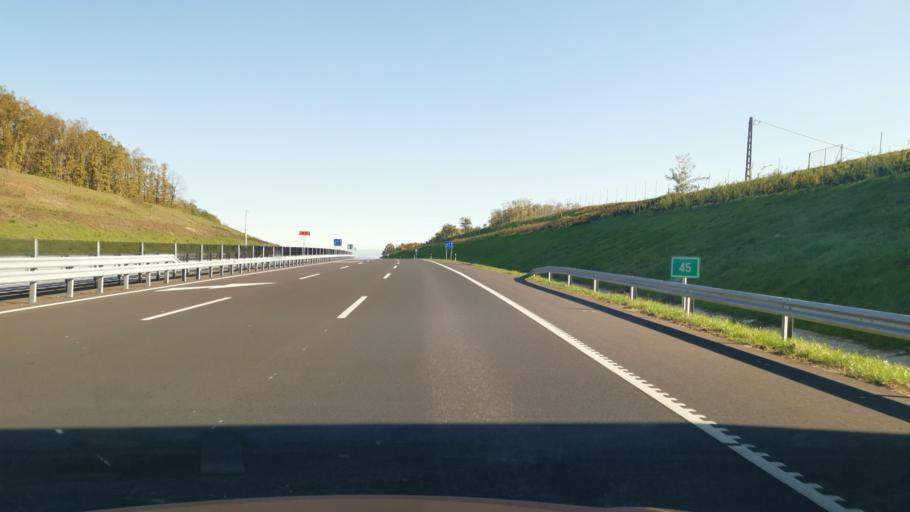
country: HU
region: Borsod-Abauj-Zemplen
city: Szikszo
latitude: 48.2175
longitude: 20.9331
